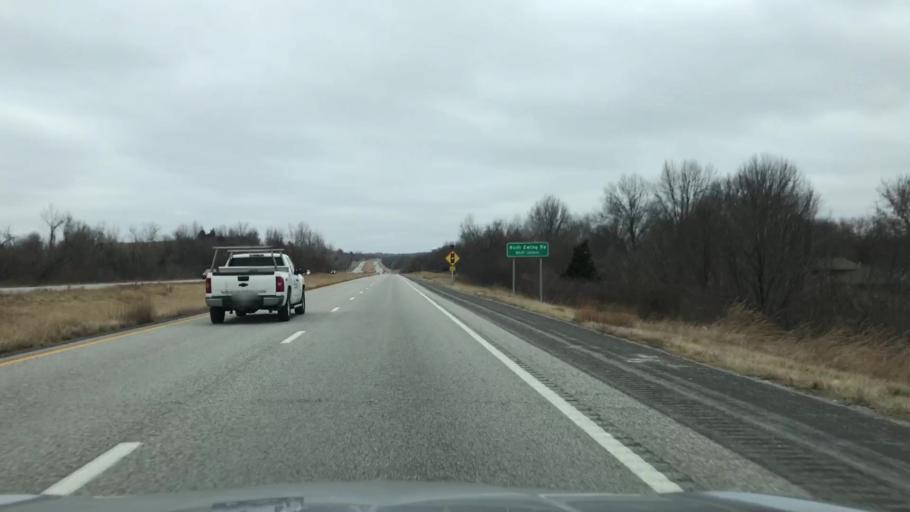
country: US
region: Missouri
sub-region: Clay County
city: Liberty
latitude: 39.2087
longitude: -94.4053
